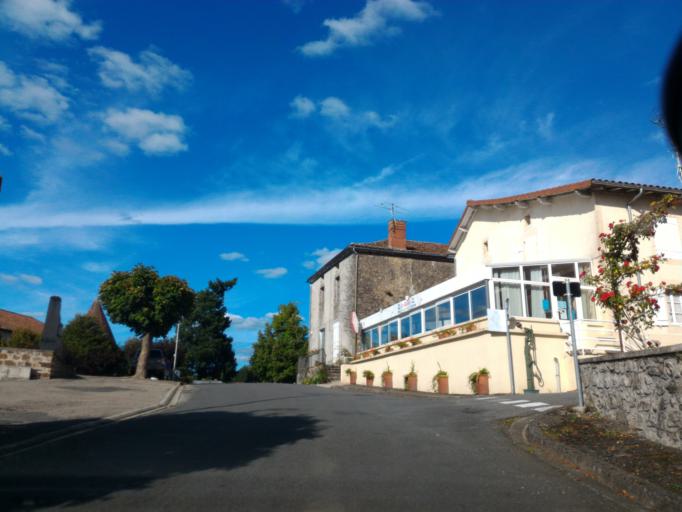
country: FR
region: Poitou-Charentes
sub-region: Departement de la Charente
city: Brigueuil
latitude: 46.0026
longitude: 0.8498
